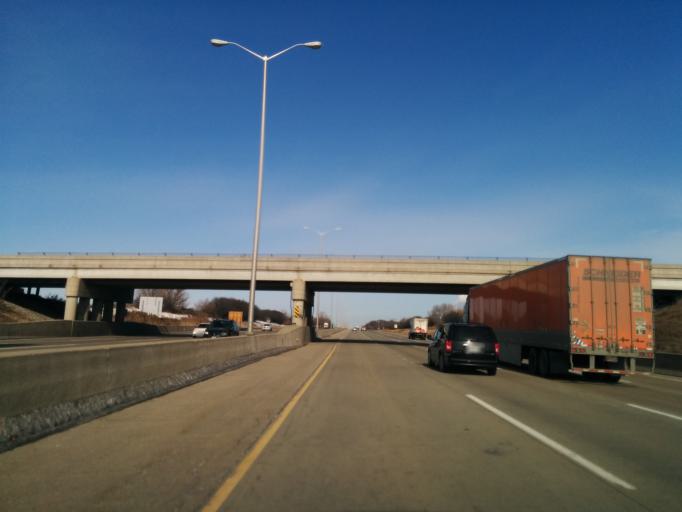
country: US
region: Illinois
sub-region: Lake County
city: Grandwood Park
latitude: 42.3929
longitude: -87.9490
